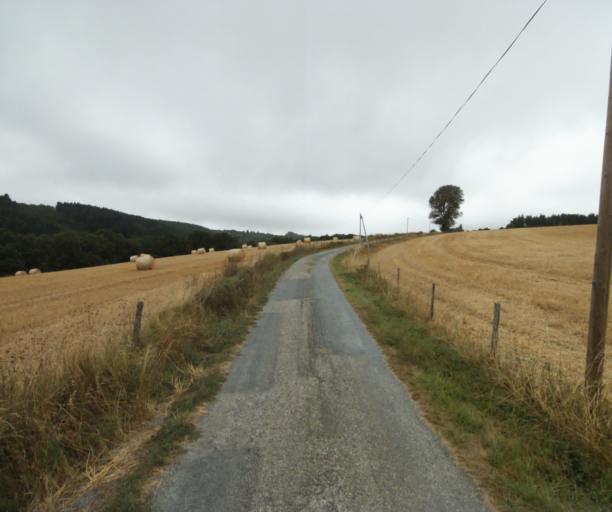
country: FR
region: Midi-Pyrenees
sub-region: Departement du Tarn
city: Soreze
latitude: 43.3997
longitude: 2.0399
